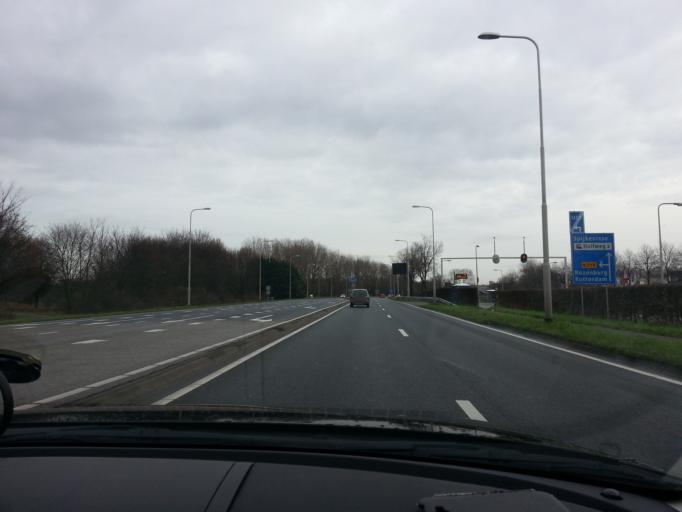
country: NL
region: South Holland
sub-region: Gemeente Spijkenisse
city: Spijkenisse
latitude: 51.8588
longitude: 4.2946
